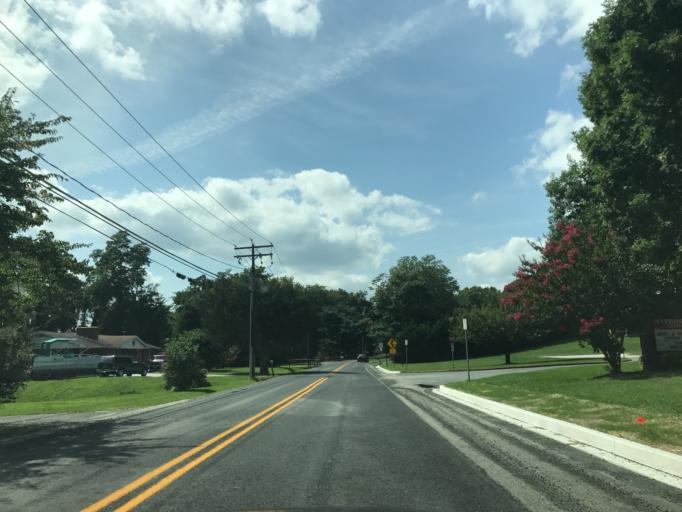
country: US
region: Maryland
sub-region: Harford County
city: South Bel Air
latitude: 39.5557
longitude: -76.2930
